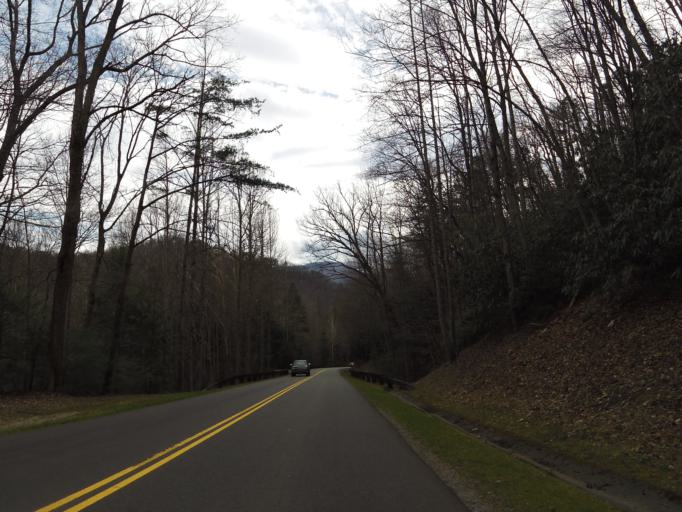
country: US
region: Tennessee
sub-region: Sevier County
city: Gatlinburg
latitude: 35.7012
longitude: -83.5291
